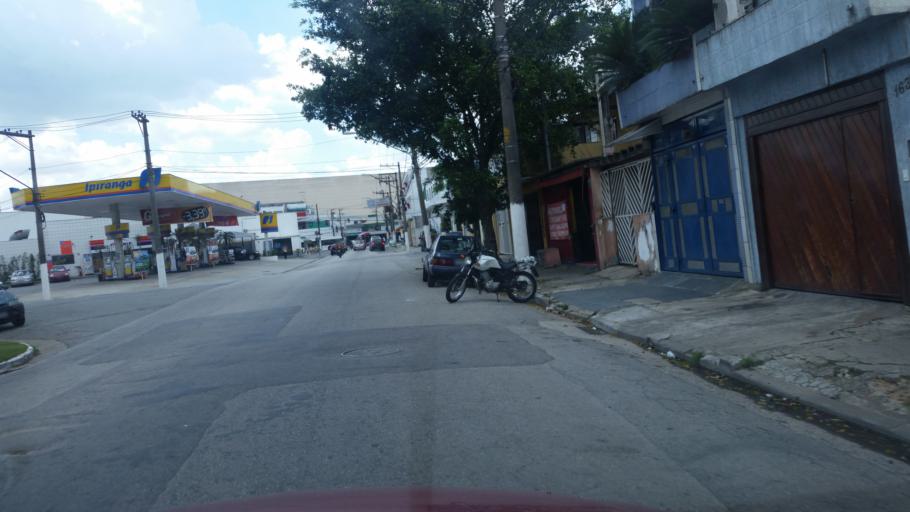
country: BR
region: Sao Paulo
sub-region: Diadema
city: Diadema
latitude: -23.6645
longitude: -46.7068
